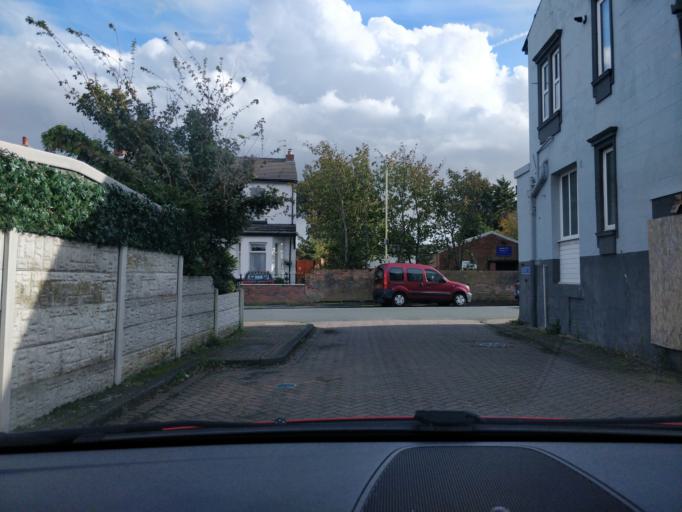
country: GB
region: England
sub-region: Sefton
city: Southport
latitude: 53.6358
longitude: -3.0070
